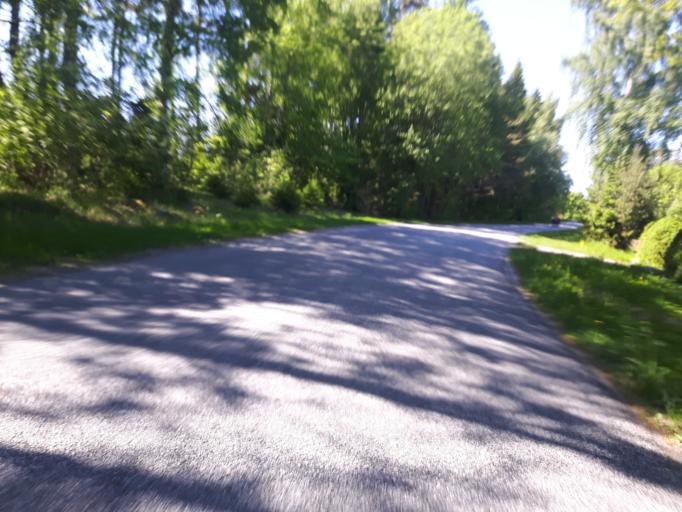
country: EE
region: Laeaene-Virumaa
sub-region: Haljala vald
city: Haljala
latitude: 59.5624
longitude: 26.3113
